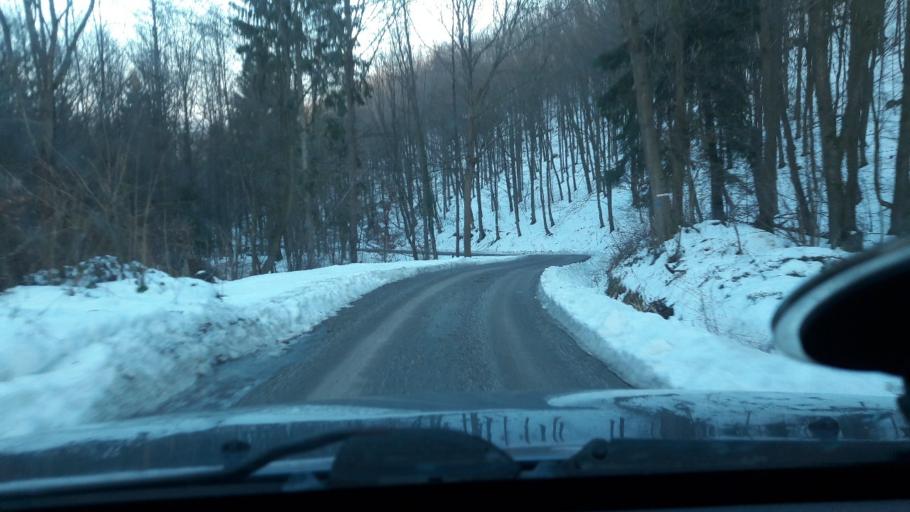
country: SK
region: Banskobystricky
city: Zarnovica
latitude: 48.5070
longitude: 18.7207
